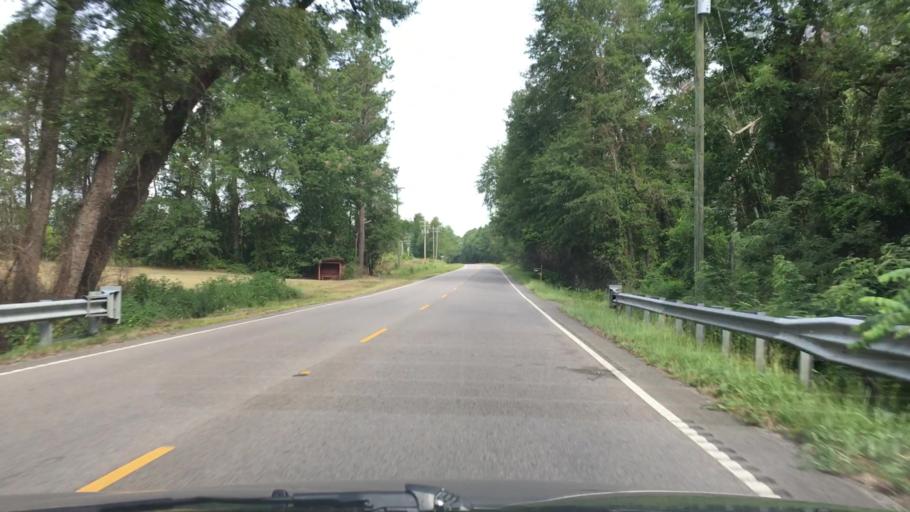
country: US
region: South Carolina
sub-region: Barnwell County
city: Williston
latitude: 33.6562
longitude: -81.3758
